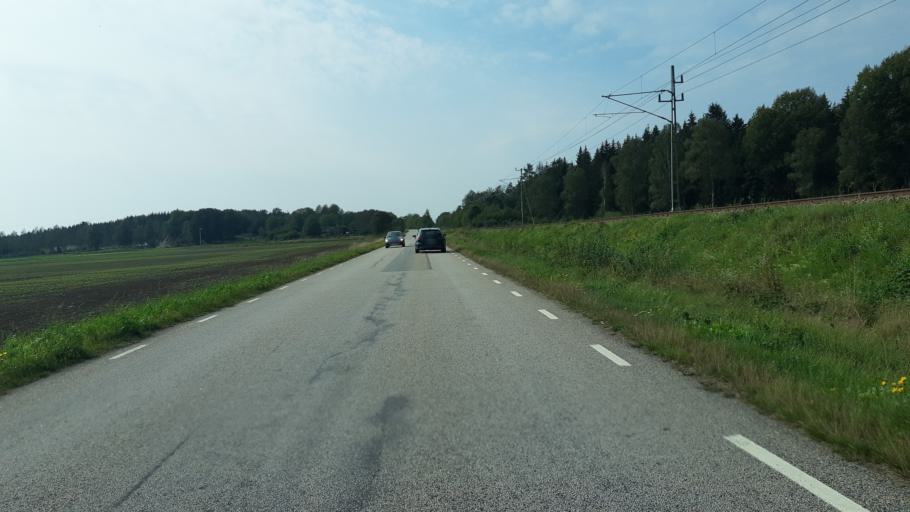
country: SE
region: Blekinge
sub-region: Ronneby Kommun
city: Kallinge
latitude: 56.2213
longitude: 15.3783
